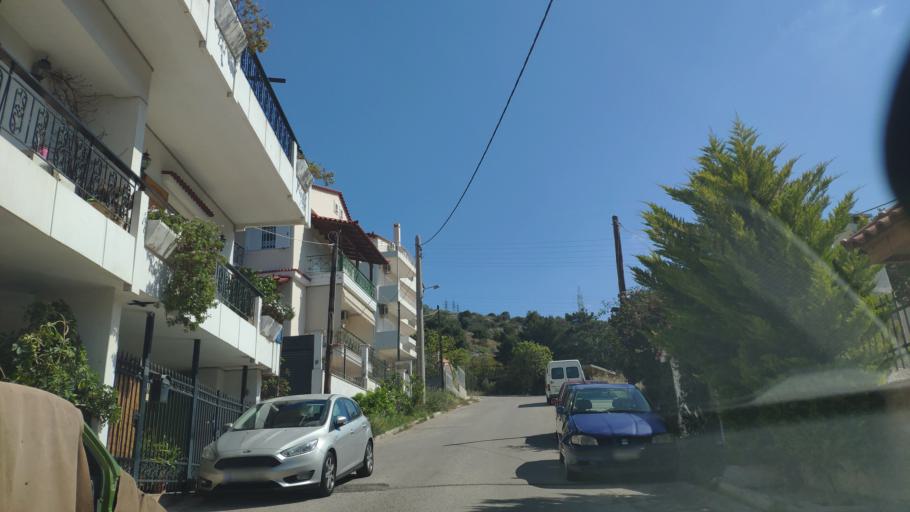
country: GR
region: Attica
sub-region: Nomarchia Athinas
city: Skaramangas
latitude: 38.0151
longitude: 23.6161
